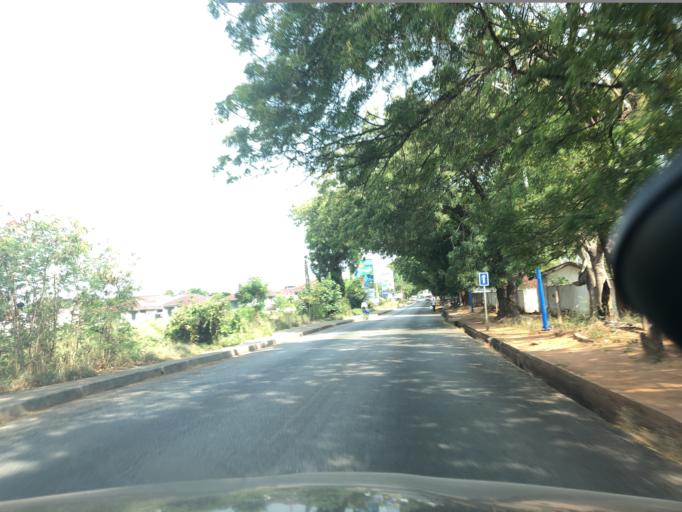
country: GH
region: Greater Accra
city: Accra
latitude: 5.5828
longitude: -0.1764
